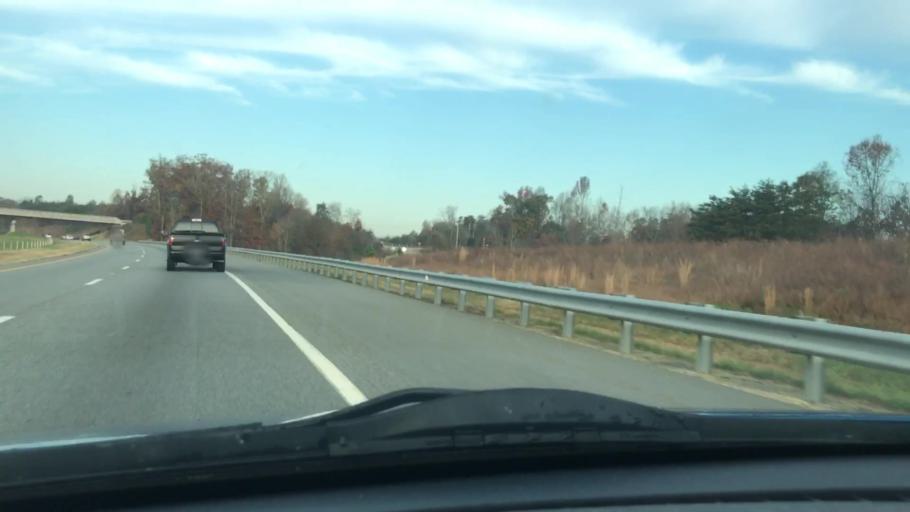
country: US
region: North Carolina
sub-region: Randolph County
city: Archdale
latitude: 35.9358
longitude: -79.9333
